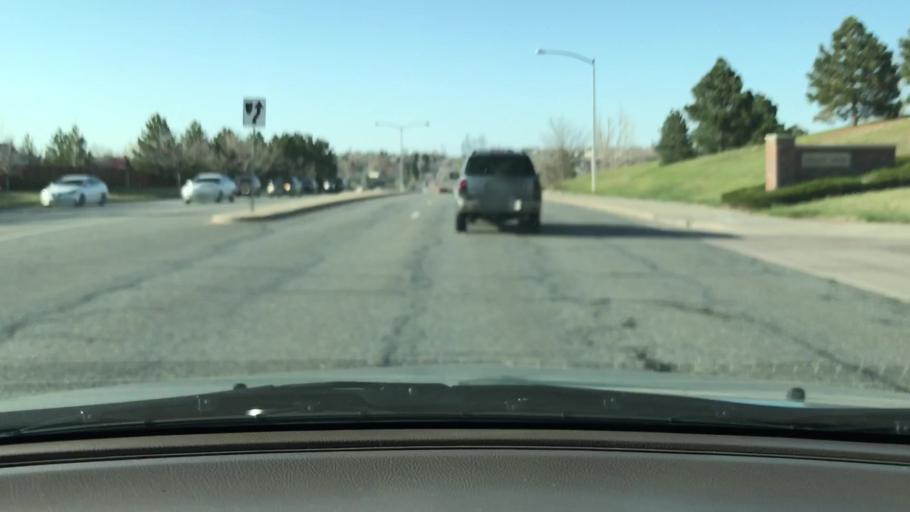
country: US
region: Colorado
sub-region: Adams County
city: Aurora
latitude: 39.6635
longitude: -104.7723
